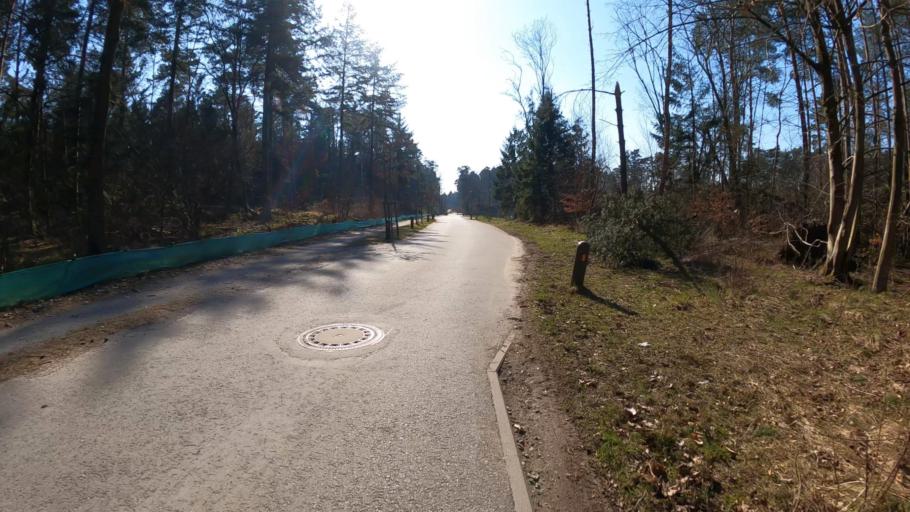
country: DE
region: Lower Saxony
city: Buchholz in der Nordheide
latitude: 53.3159
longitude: 9.8543
